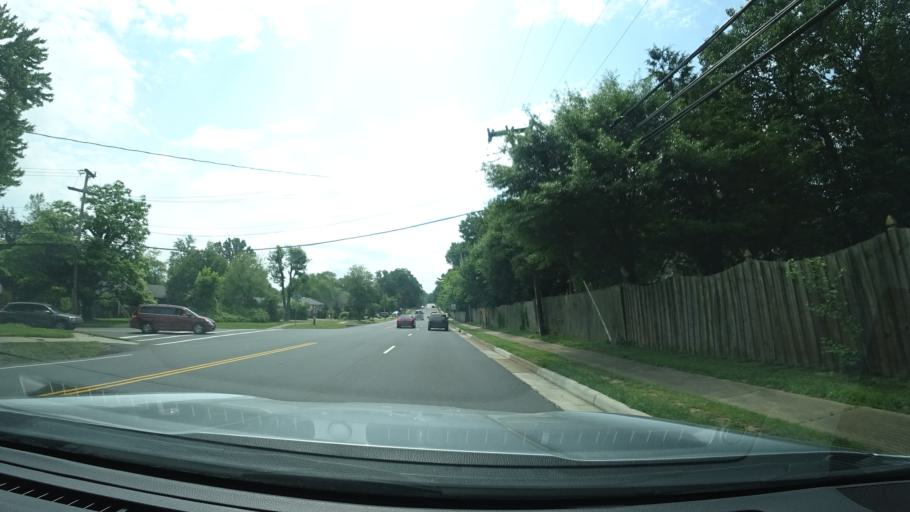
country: US
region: Virginia
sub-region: Loudoun County
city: Oak Grove
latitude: 38.9725
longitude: -77.4006
